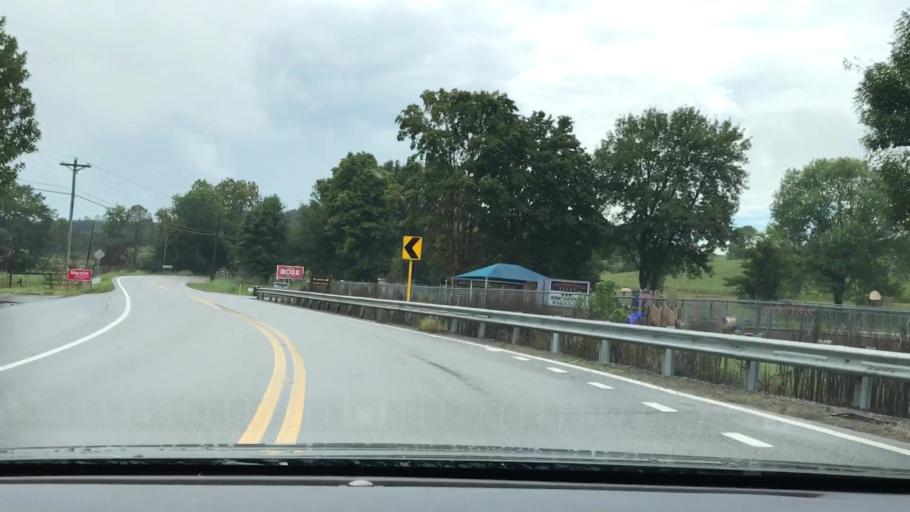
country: US
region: Tennessee
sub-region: Macon County
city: Red Boiling Springs
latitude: 36.5755
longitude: -85.7809
